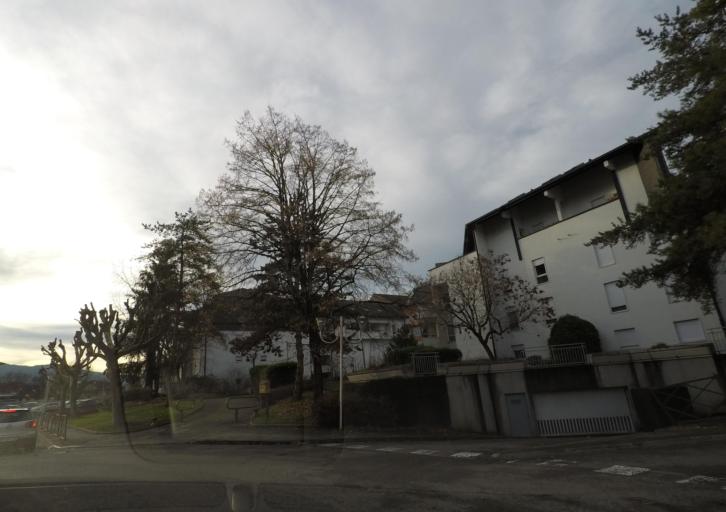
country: FR
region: Rhone-Alpes
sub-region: Departement de la Haute-Savoie
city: Bonneville
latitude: 46.0746
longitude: 6.4083
